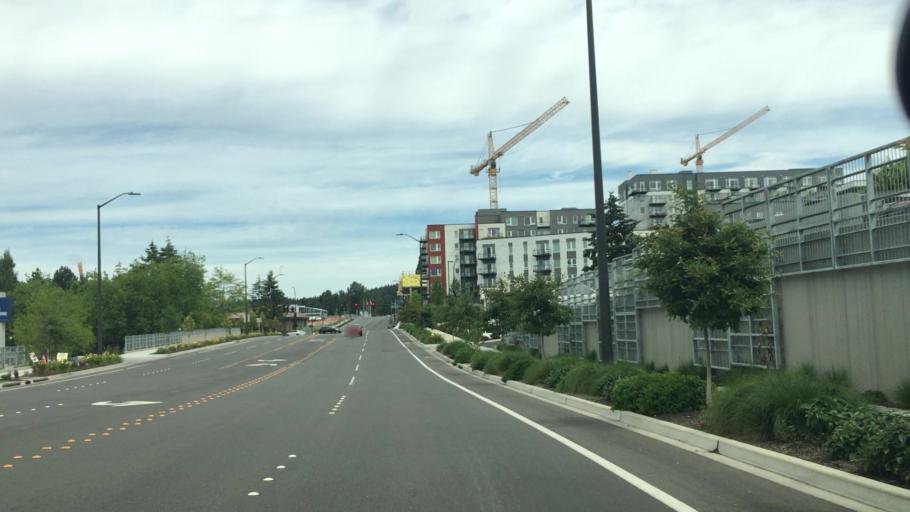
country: US
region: Washington
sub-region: King County
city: Bellevue
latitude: 47.6190
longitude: -122.1792
